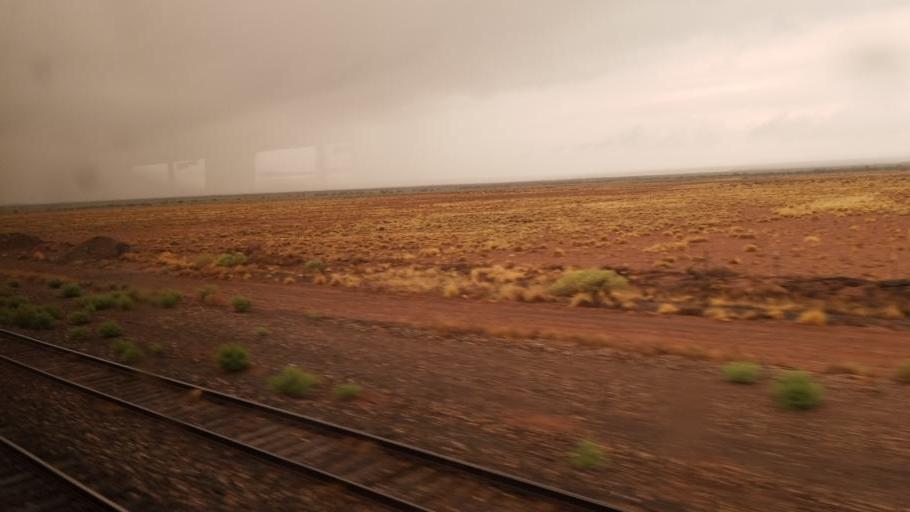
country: US
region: Arizona
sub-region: Navajo County
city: Joseph City
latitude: 34.9676
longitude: -110.5157
